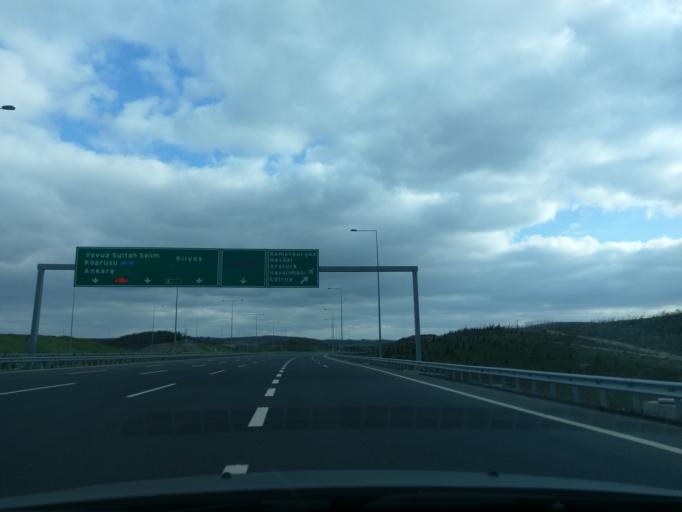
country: TR
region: Istanbul
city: Kemerburgaz
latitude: 41.2371
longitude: 28.8323
